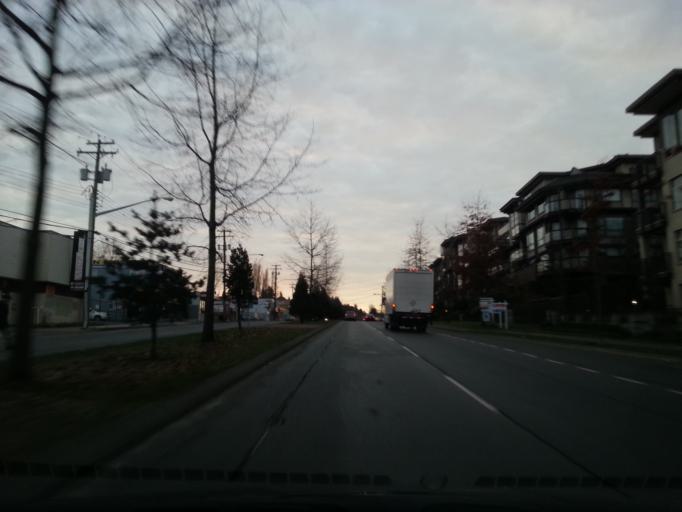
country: CA
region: British Columbia
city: New Westminster
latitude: 49.2013
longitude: -122.8490
